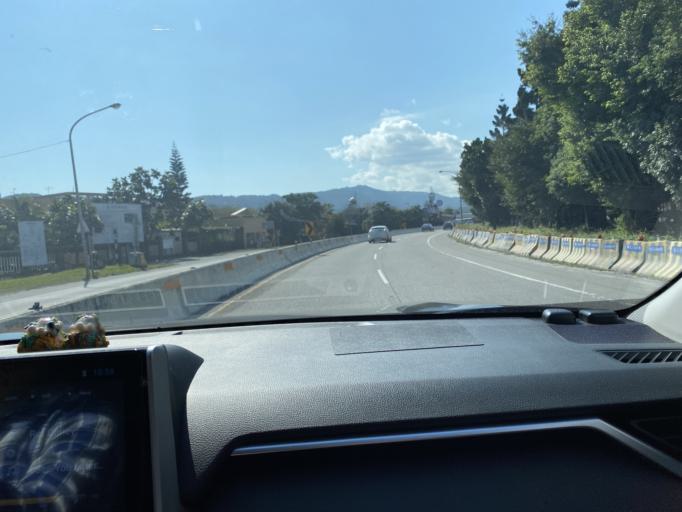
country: TW
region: Taiwan
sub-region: Hualien
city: Hualian
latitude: 23.9321
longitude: 121.5946
